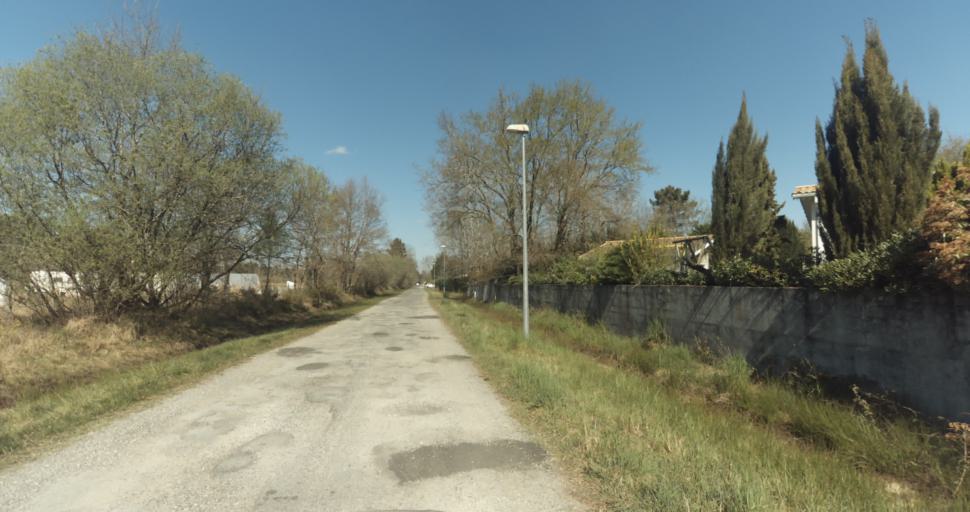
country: FR
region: Aquitaine
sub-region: Departement de la Gironde
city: Martignas-sur-Jalle
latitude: 44.7970
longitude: -0.7880
